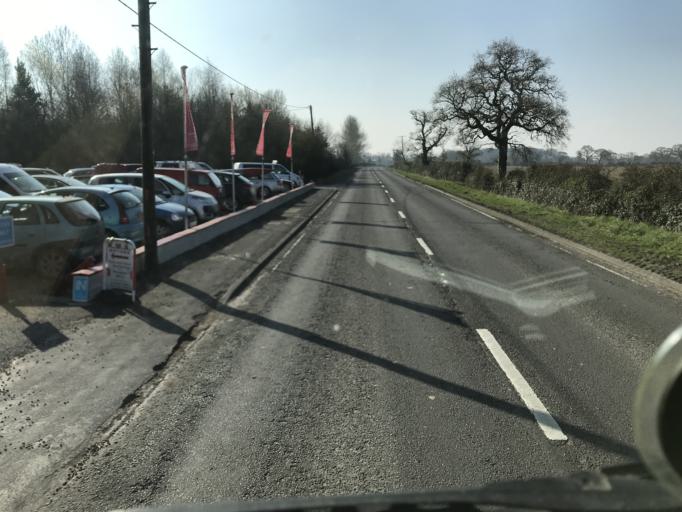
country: GB
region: England
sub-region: Cheshire West and Chester
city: Waverton
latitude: 53.1509
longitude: -2.8118
